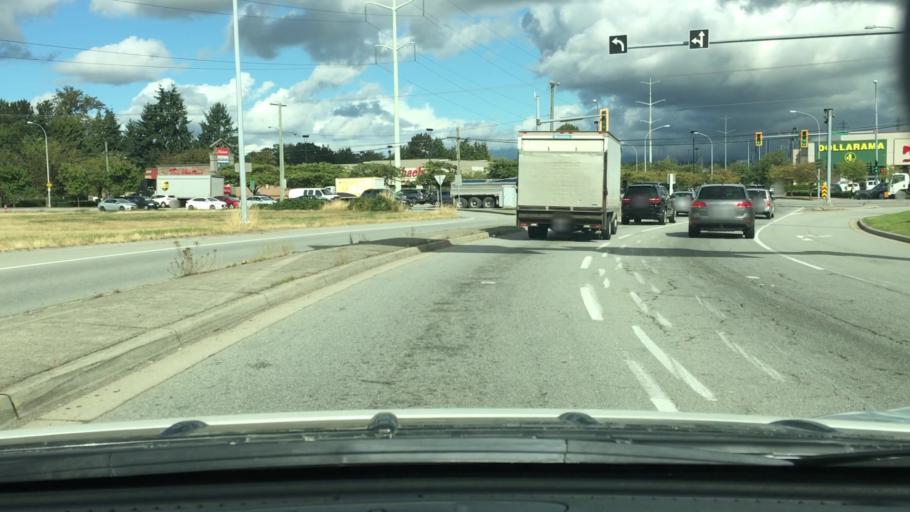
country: CA
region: British Columbia
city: Richmond
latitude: 49.1912
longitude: -123.1150
